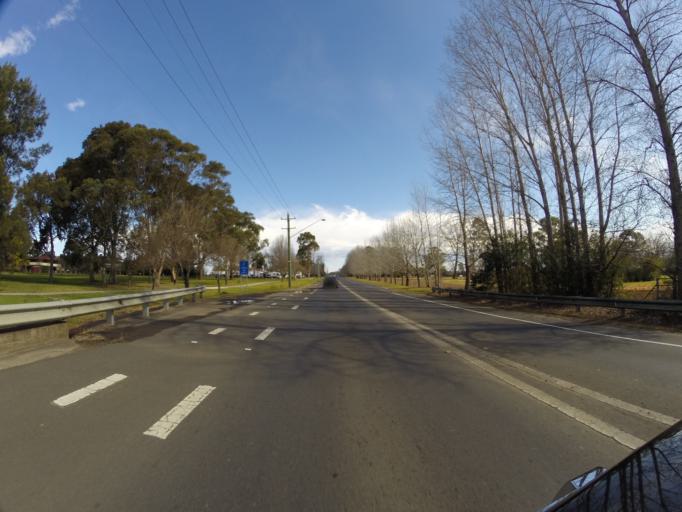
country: AU
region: New South Wales
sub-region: Camden
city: Elderslie
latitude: -34.0504
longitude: 150.7132
